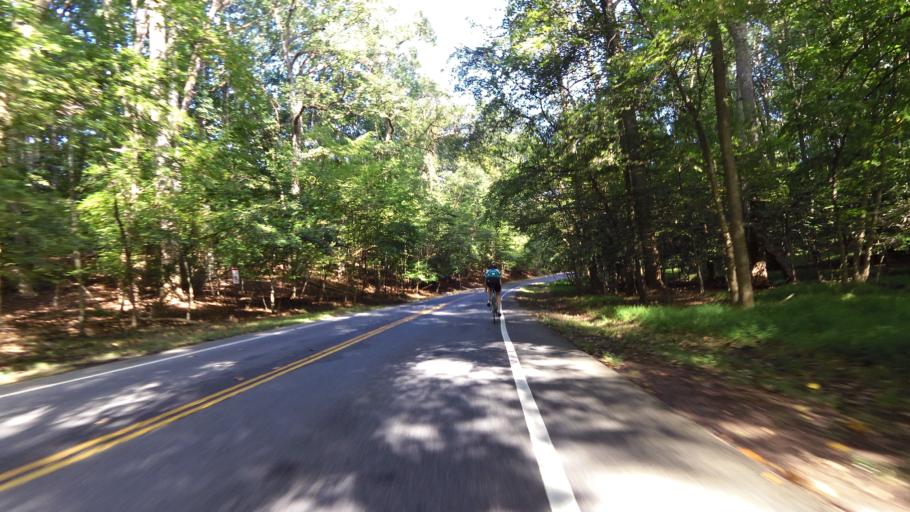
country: US
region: Maryland
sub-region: Montgomery County
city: Potomac
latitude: 38.9995
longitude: -77.2388
